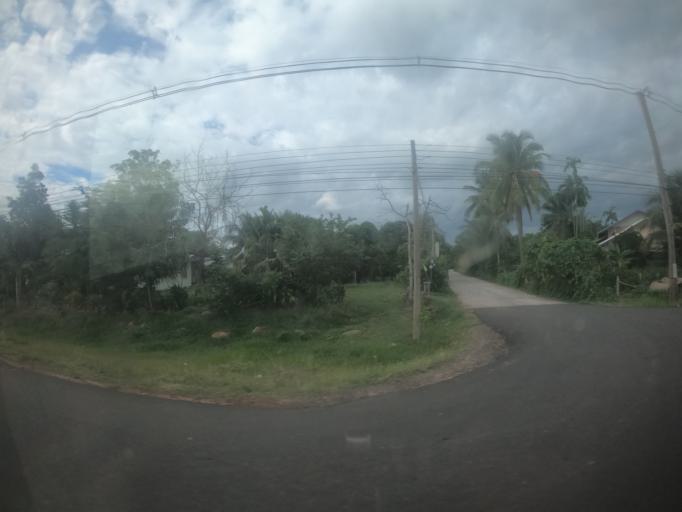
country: TH
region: Surin
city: Prasat
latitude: 14.5651
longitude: 103.4939
